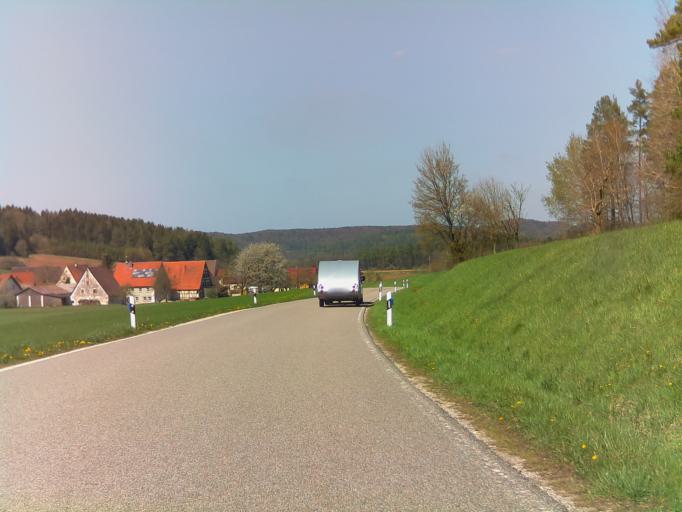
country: DE
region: Bavaria
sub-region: Upper Palatinate
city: Weigendorf
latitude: 49.4741
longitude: 11.5571
